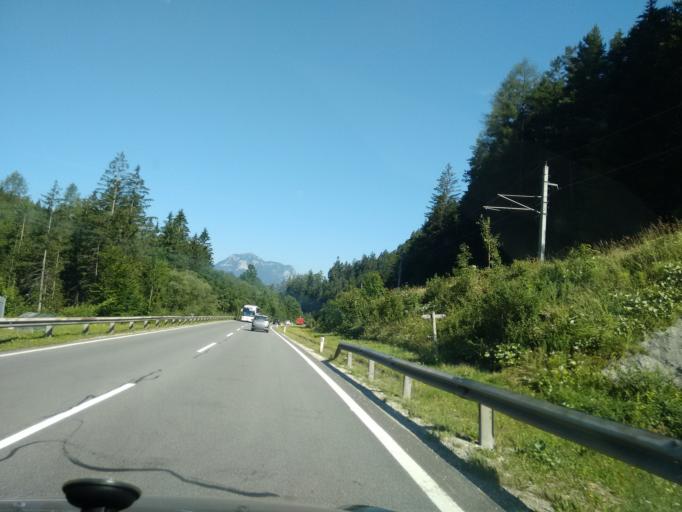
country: AT
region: Styria
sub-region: Politischer Bezirk Liezen
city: Bad Aussee
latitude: 47.5869
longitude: 13.8016
